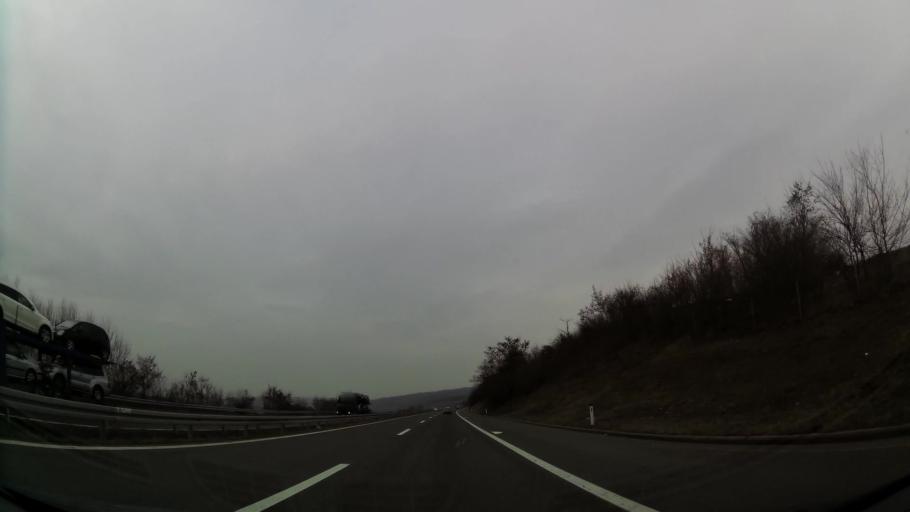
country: RS
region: Central Serbia
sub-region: Nisavski Okrug
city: Aleksinac
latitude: 43.4268
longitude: 21.7975
